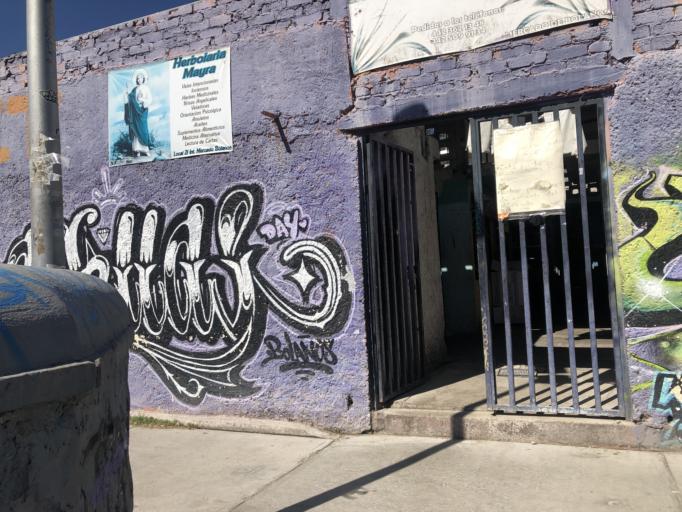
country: MX
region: Queretaro
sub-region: Queretaro
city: Santiago de Queretaro
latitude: 20.6141
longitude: -100.3741
